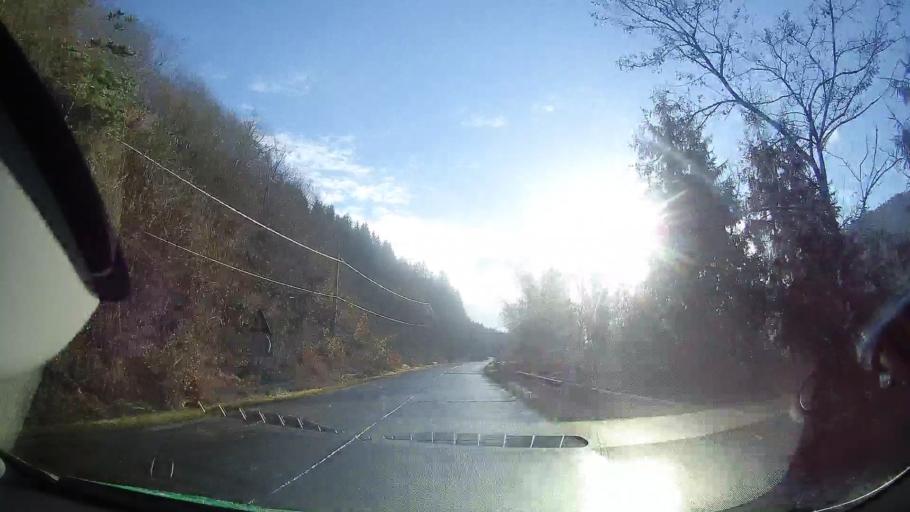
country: RO
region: Alba
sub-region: Comuna Vadu Motilor
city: Vadu Motilor
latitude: 46.3927
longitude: 22.9946
